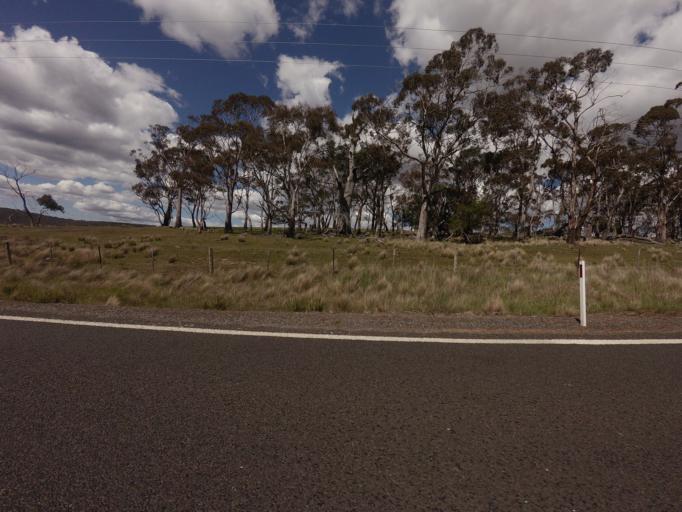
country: AU
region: Tasmania
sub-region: Northern Midlands
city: Evandale
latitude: -41.9436
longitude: 147.6042
